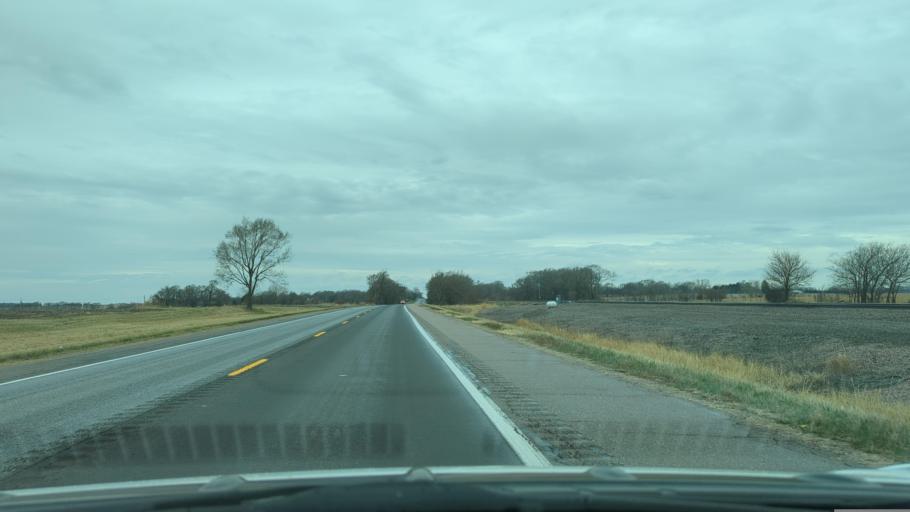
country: US
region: Nebraska
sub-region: Saunders County
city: Ashland
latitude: 40.9739
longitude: -96.4301
